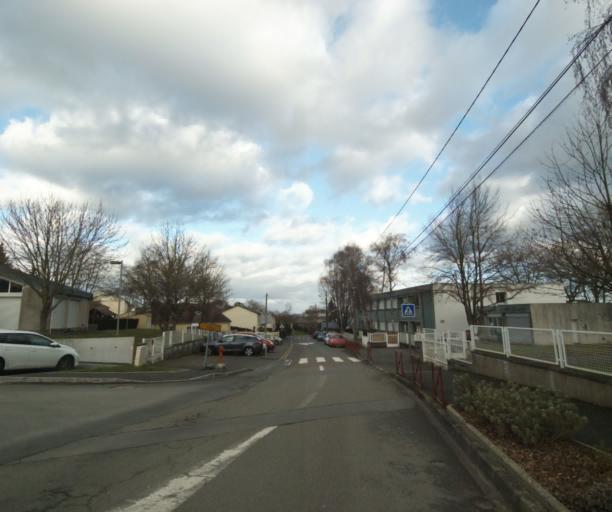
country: FR
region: Pays de la Loire
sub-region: Departement de la Sarthe
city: Allonnes
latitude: 47.9901
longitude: 0.1641
